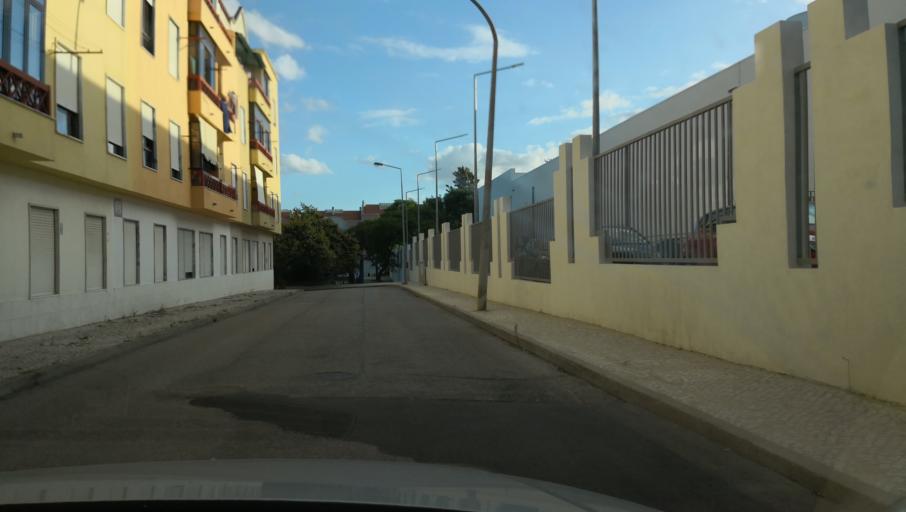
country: PT
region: Setubal
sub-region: Barreiro
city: Barreiro
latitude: 38.6671
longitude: -9.0476
